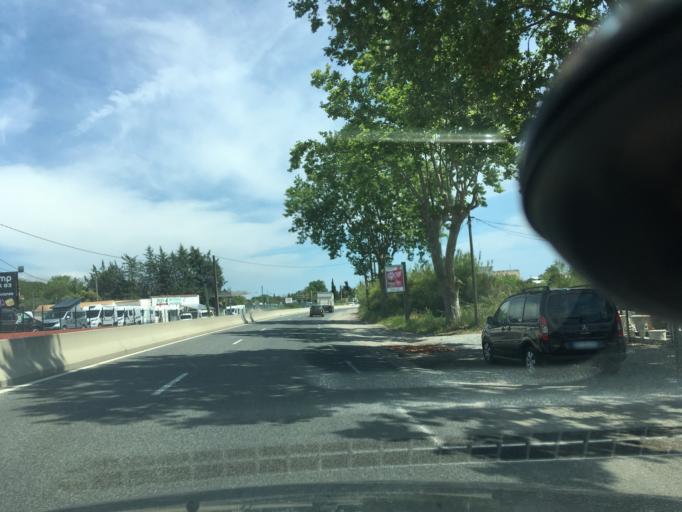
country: FR
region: Provence-Alpes-Cote d'Azur
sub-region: Departement du Var
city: Roquebrune-sur-Argens
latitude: 43.4638
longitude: 6.6404
